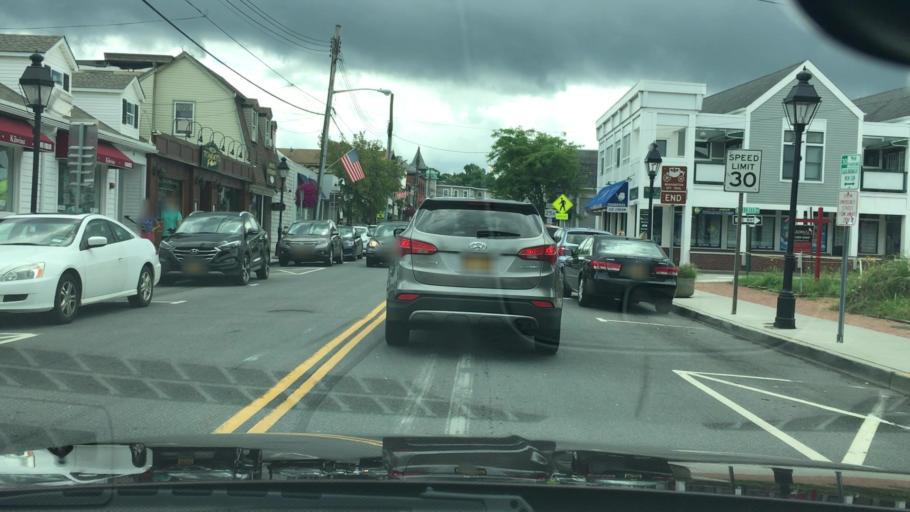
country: US
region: New York
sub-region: Suffolk County
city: Port Jefferson
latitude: 40.9463
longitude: -73.0698
